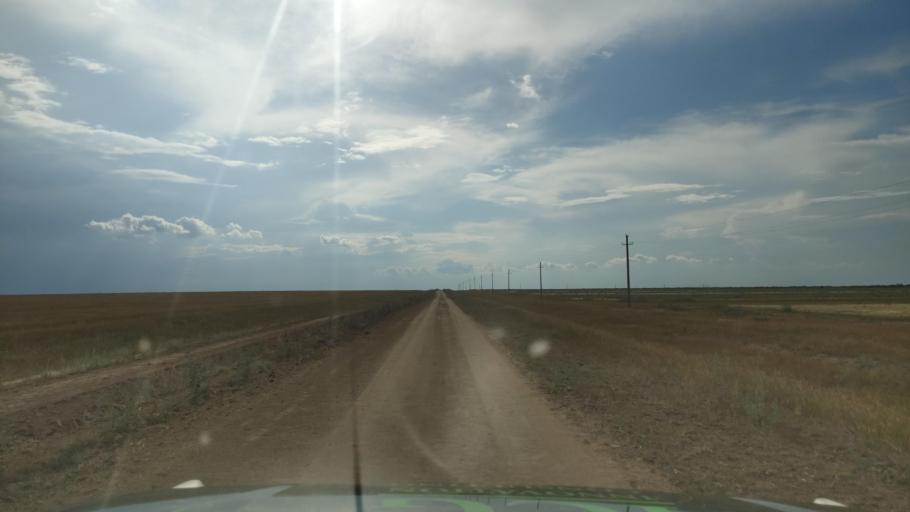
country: KZ
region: Pavlodar
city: Pavlodar
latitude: 52.5090
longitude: 77.5664
